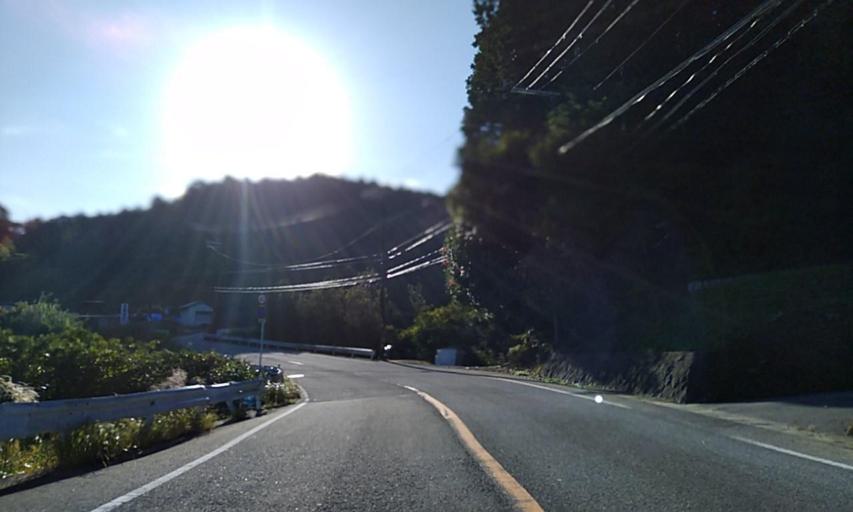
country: JP
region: Wakayama
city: Kainan
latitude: 34.1556
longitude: 135.2879
